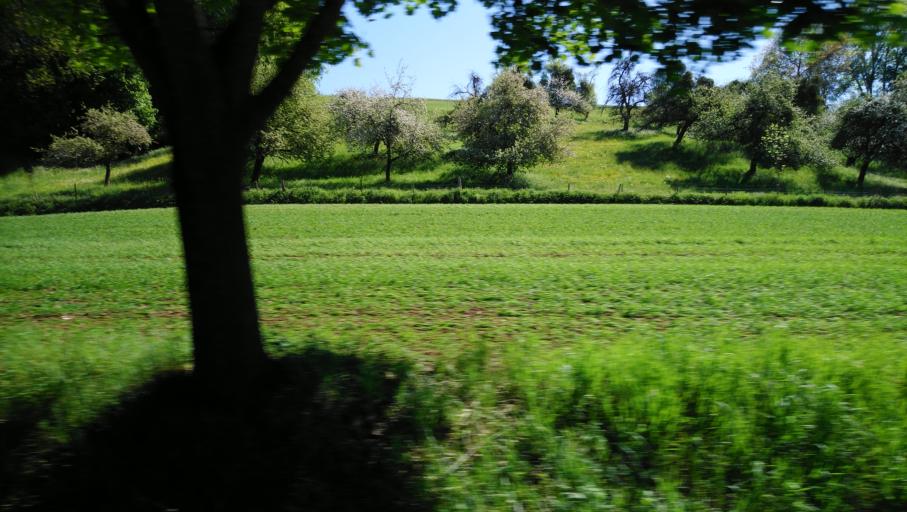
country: LU
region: Diekirch
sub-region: Canton de Vianden
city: Tandel
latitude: 49.8749
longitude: 6.1900
